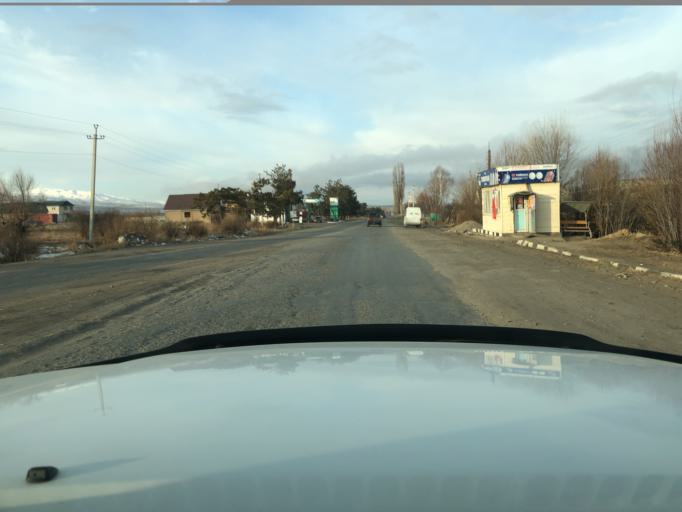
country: KG
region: Ysyk-Koel
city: Karakol
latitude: 42.4827
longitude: 78.3641
